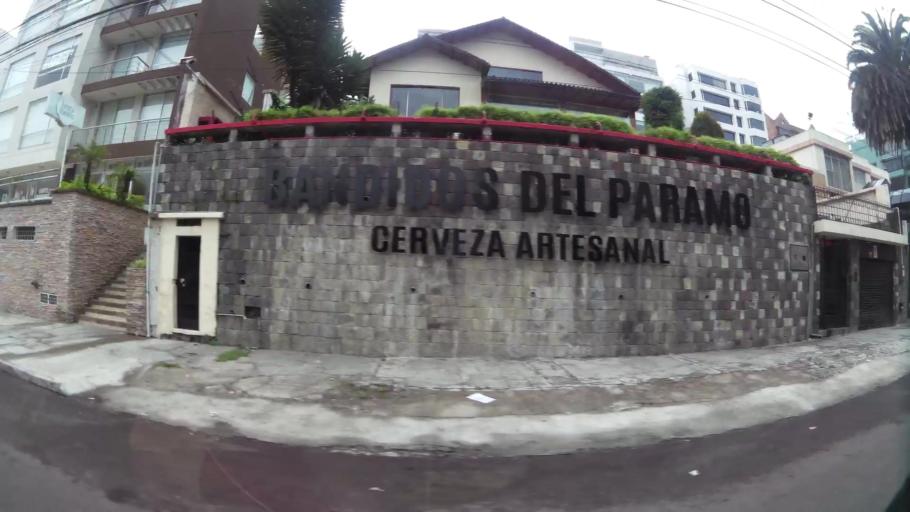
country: EC
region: Pichincha
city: Quito
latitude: -0.1983
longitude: -78.4813
